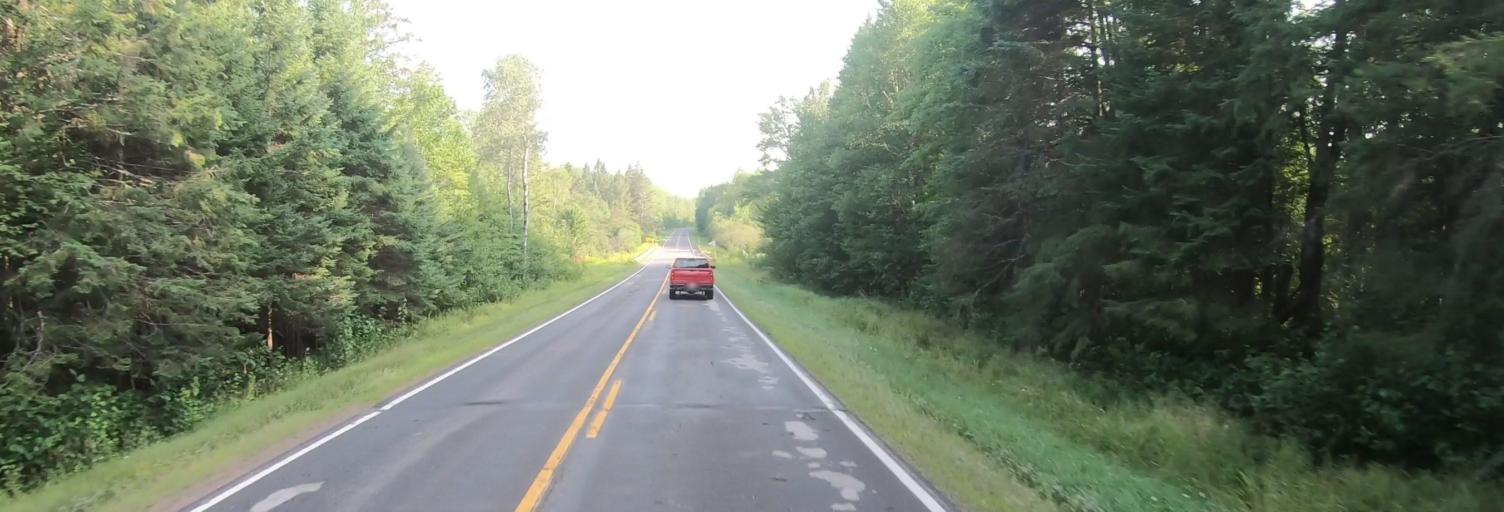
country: US
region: Wisconsin
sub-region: Ashland County
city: Ashland
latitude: 46.2366
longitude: -90.8352
